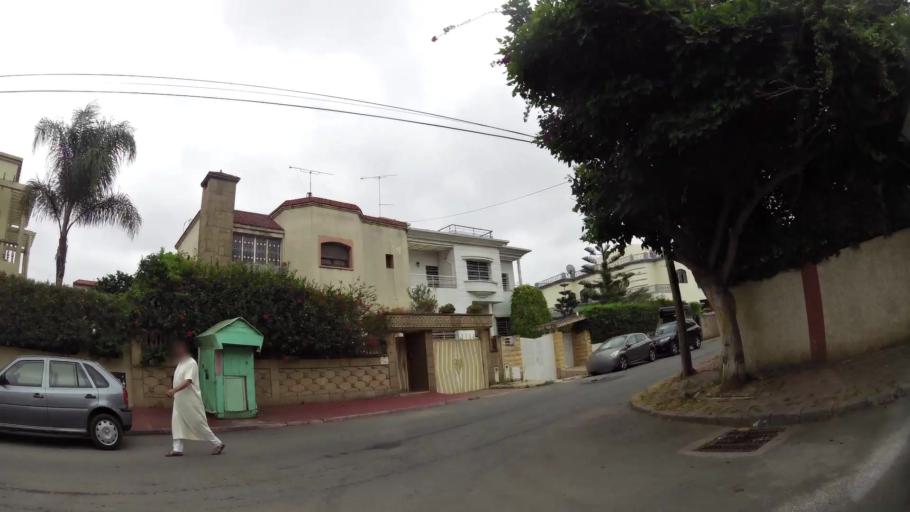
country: MA
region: Rabat-Sale-Zemmour-Zaer
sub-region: Rabat
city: Rabat
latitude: 33.9790
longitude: -6.8122
